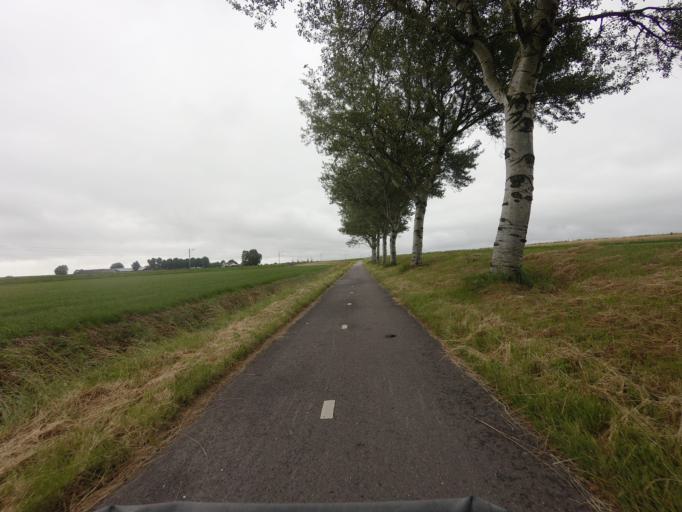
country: NL
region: North Holland
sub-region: Gemeente Schagen
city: Schagen
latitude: 52.8058
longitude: 4.8049
